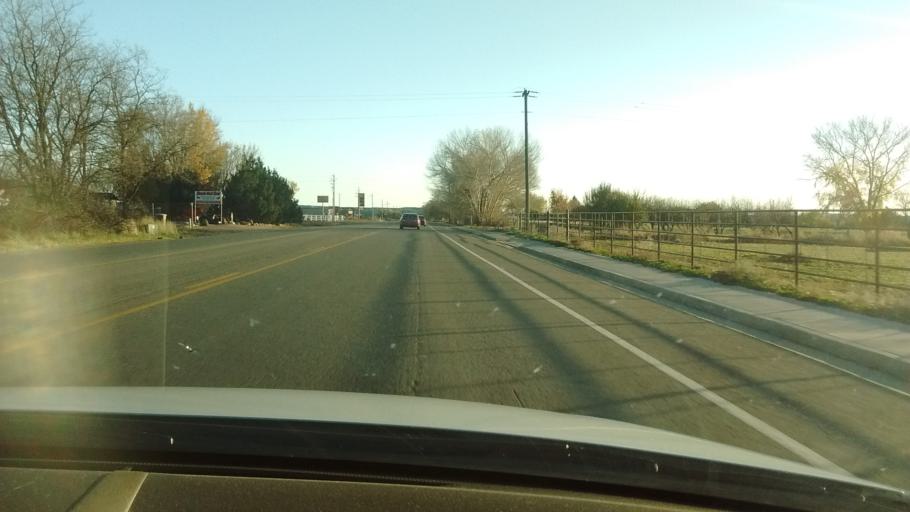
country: US
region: Utah
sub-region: Kane County
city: Kanab
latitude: 37.0337
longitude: -112.5249
